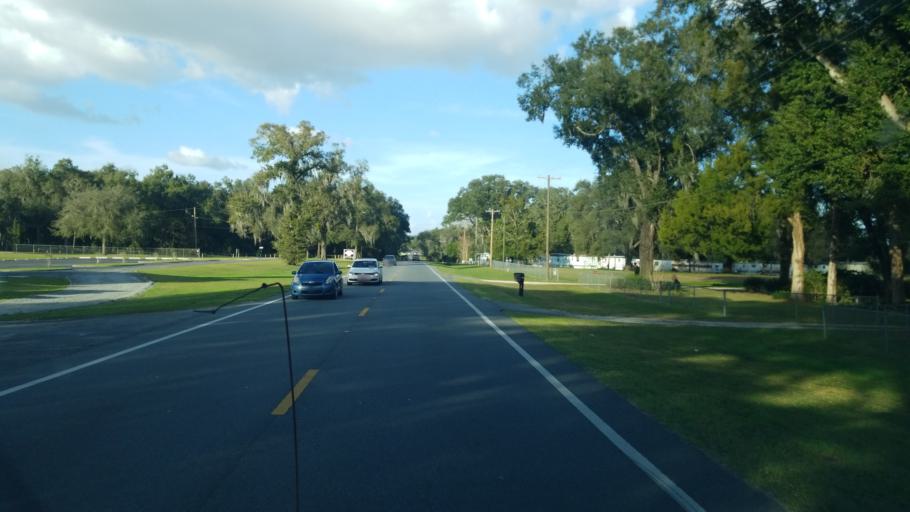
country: US
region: Florida
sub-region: Marion County
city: Ocala
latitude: 29.2531
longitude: -82.1154
